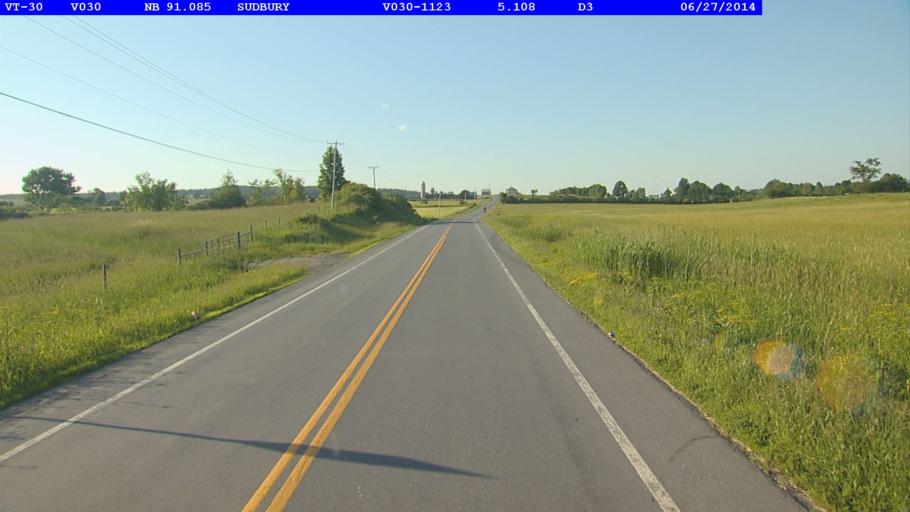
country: US
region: Vermont
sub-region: Rutland County
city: Brandon
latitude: 43.8198
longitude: -73.1936
